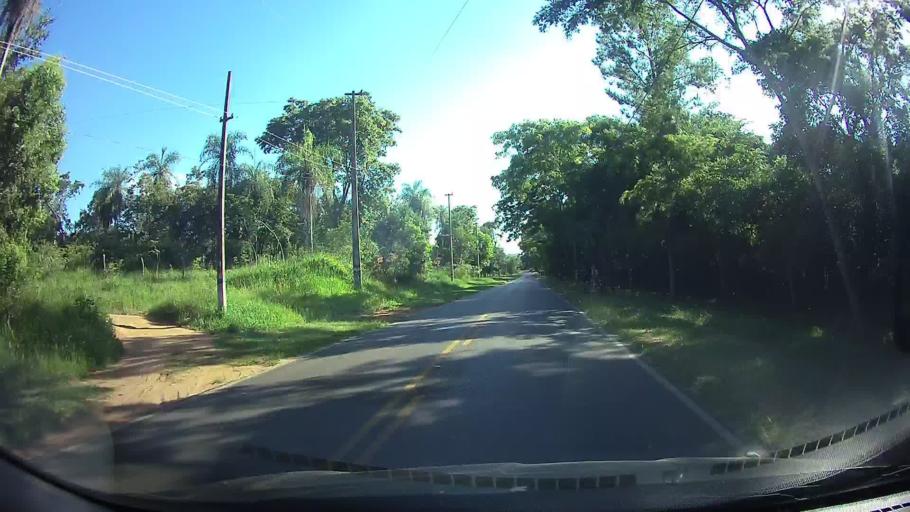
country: PY
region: Cordillera
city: Atyra
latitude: -25.2918
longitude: -57.1820
